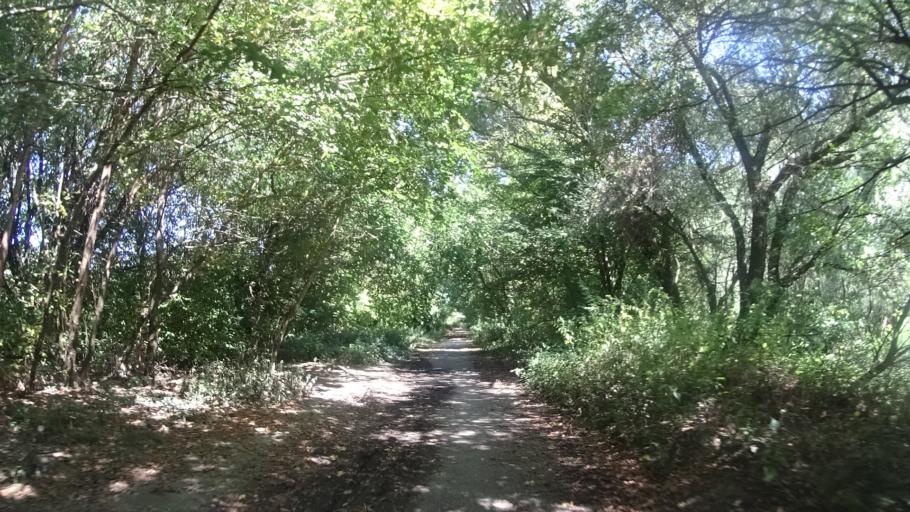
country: AT
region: Lower Austria
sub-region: Politischer Bezirk Bruck an der Leitha
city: Hainburg an der Donau
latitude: 48.1763
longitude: 16.9762
